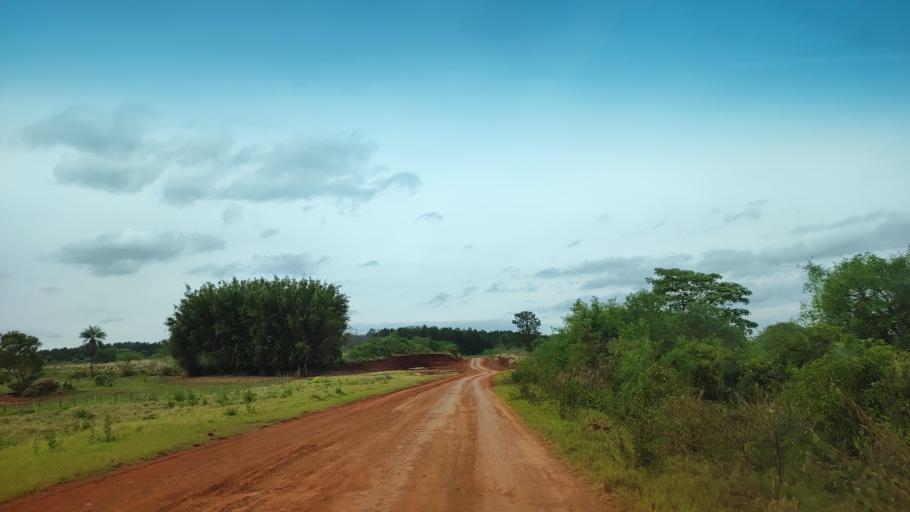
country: AR
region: Misiones
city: Garupa
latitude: -27.5166
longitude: -55.9739
